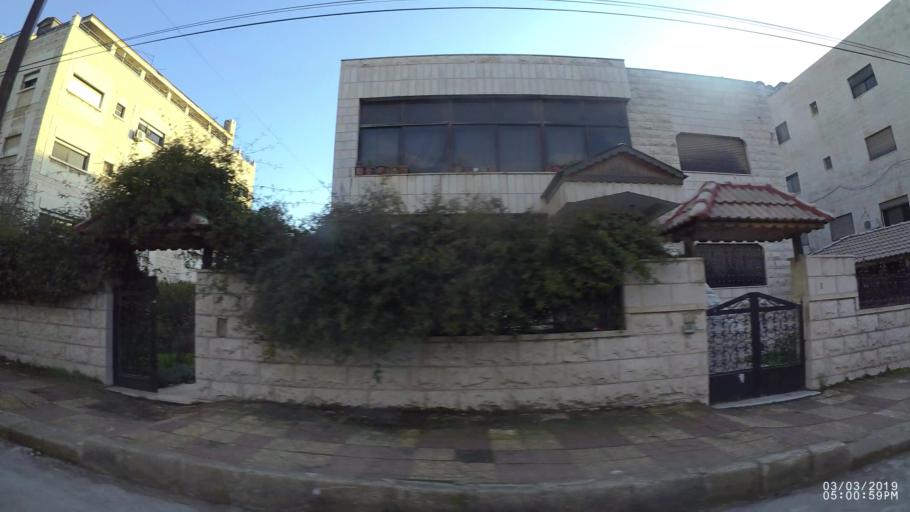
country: JO
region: Amman
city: Al Jubayhah
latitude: 31.9921
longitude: 35.8731
